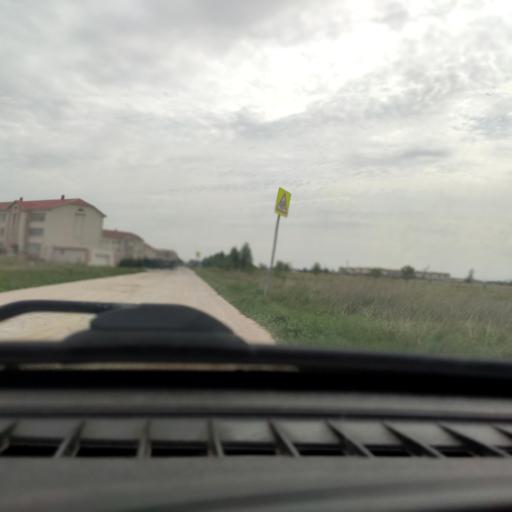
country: RU
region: Samara
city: Podstepki
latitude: 53.5279
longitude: 49.1756
